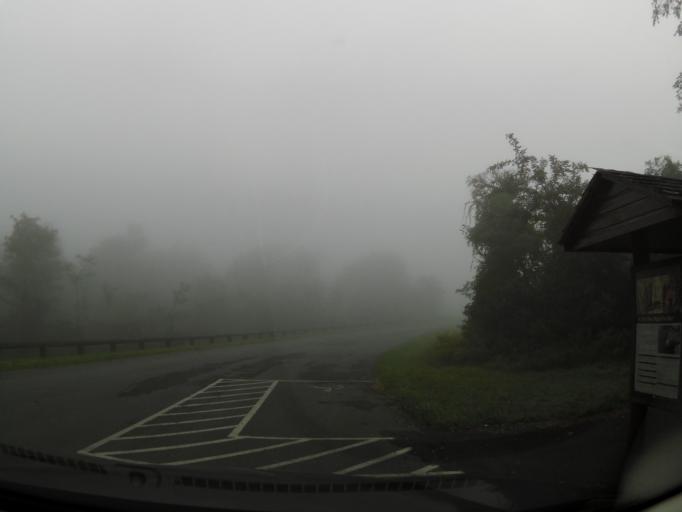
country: US
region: Virginia
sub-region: Page County
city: Luray
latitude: 38.6947
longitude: -78.3197
